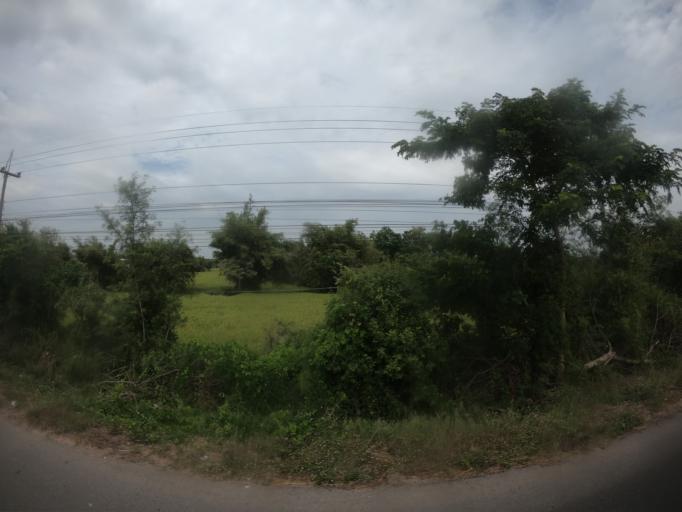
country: TH
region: Roi Et
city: Changhan
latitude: 16.0929
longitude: 103.5441
